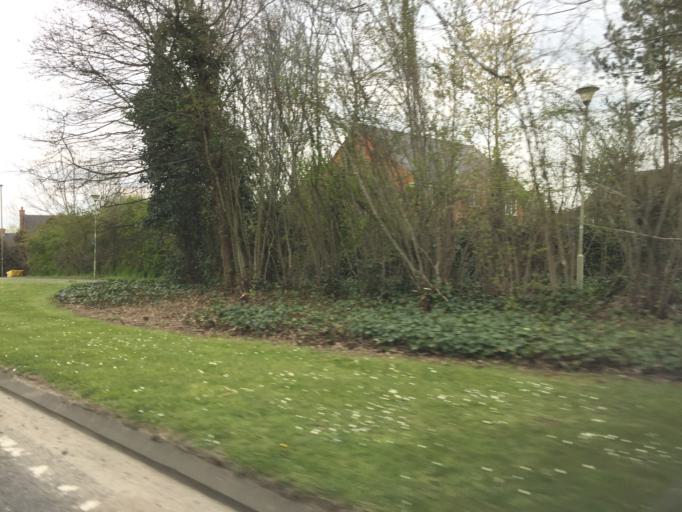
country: GB
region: England
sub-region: Oxfordshire
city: Bicester
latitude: 51.9124
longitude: -1.1657
